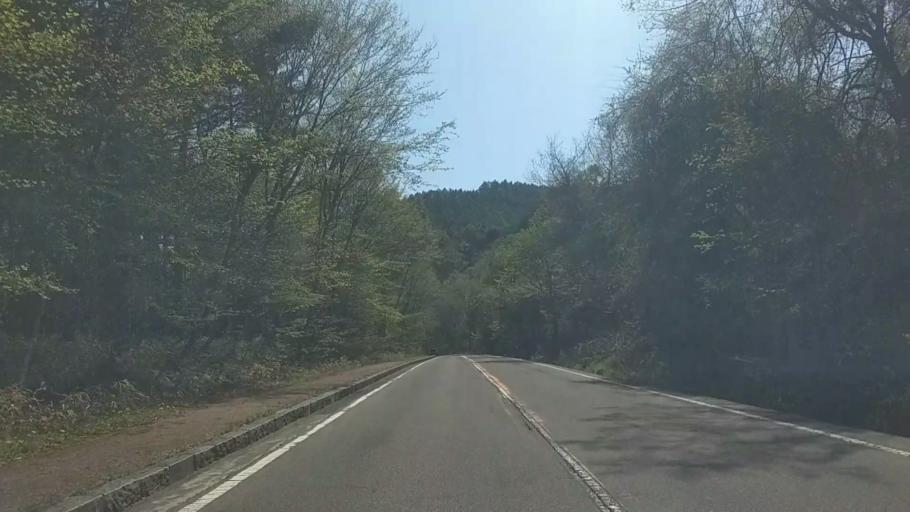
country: JP
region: Yamanashi
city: Nirasaki
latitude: 35.9231
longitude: 138.4071
